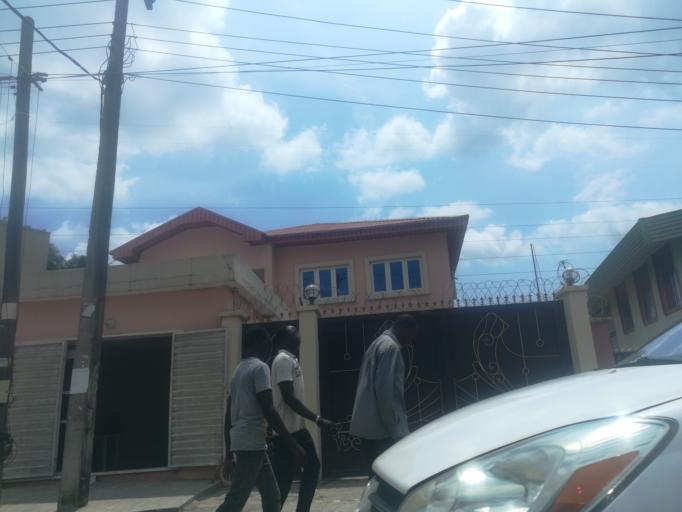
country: NG
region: Lagos
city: Somolu
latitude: 6.5588
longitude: 3.3857
